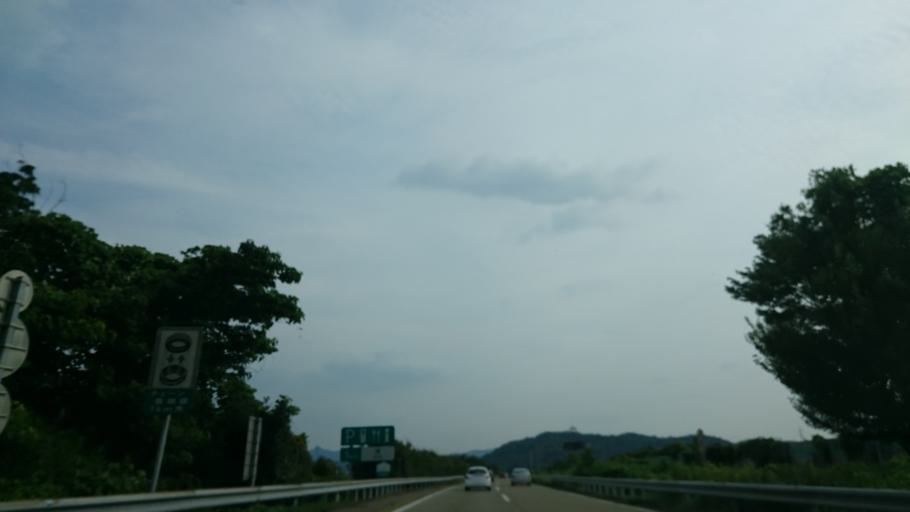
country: JP
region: Gifu
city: Mino
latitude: 35.5002
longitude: 136.8987
